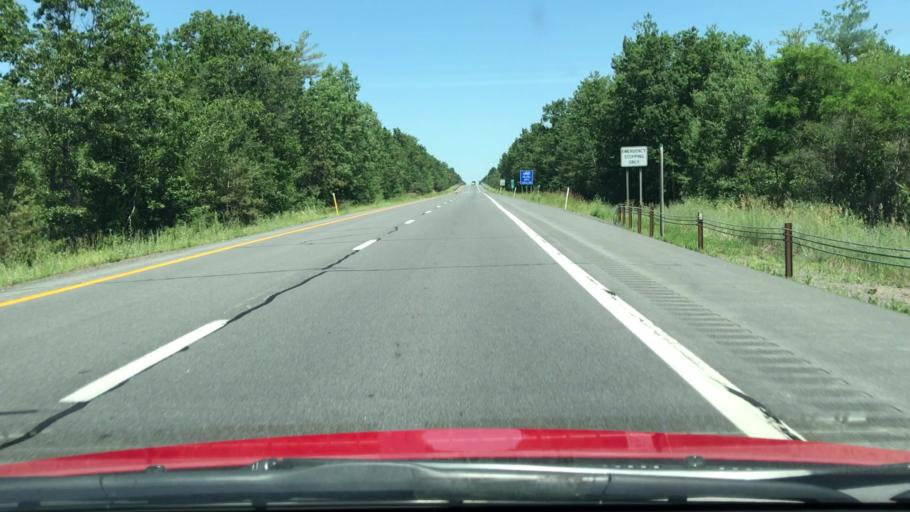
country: US
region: New York
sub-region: Essex County
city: Keeseville
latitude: 44.5003
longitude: -73.5009
